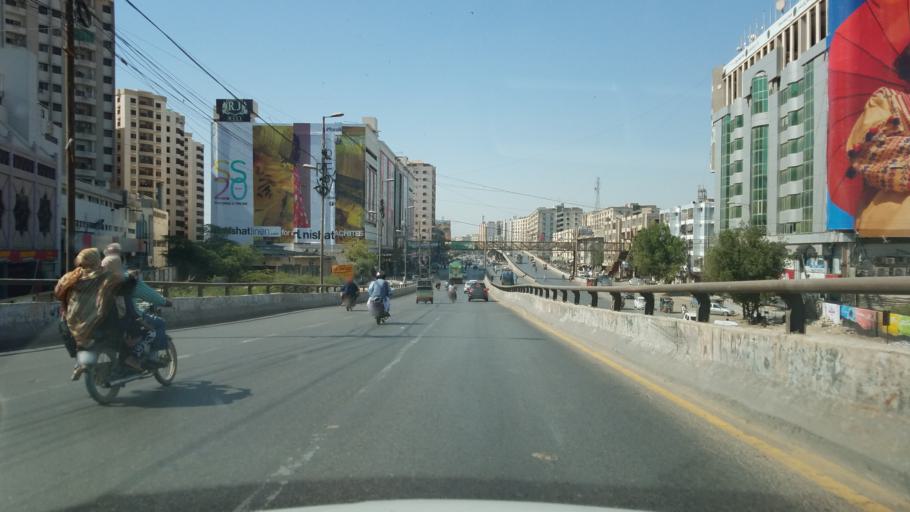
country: PK
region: Sindh
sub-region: Karachi District
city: Karachi
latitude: 24.9015
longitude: 67.1159
